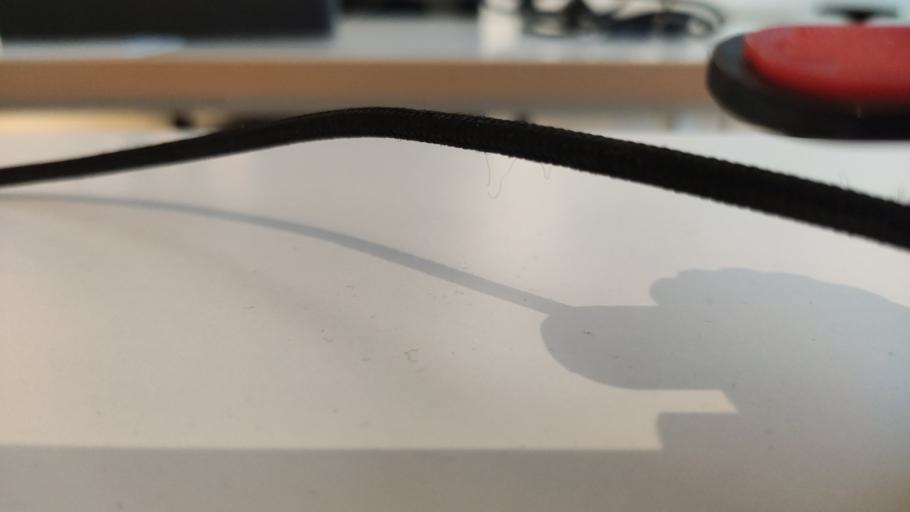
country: RU
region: Moskovskaya
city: Novopetrovskoye
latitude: 55.9051
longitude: 36.4414
